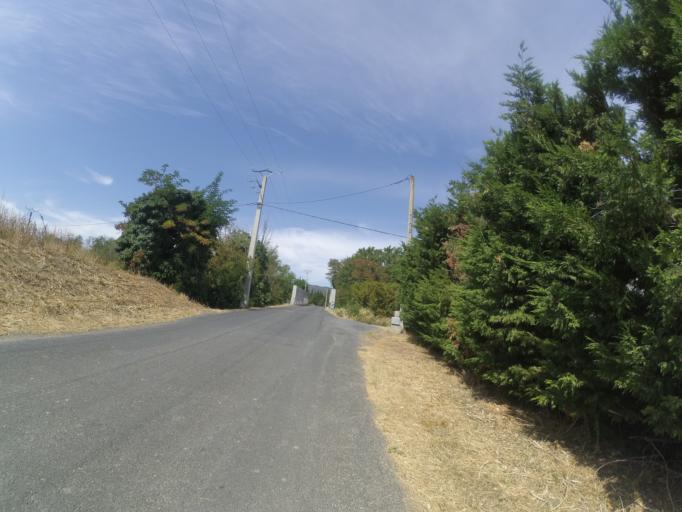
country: FR
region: Languedoc-Roussillon
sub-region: Departement des Pyrenees-Orientales
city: Millas
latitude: 42.6804
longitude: 2.6683
